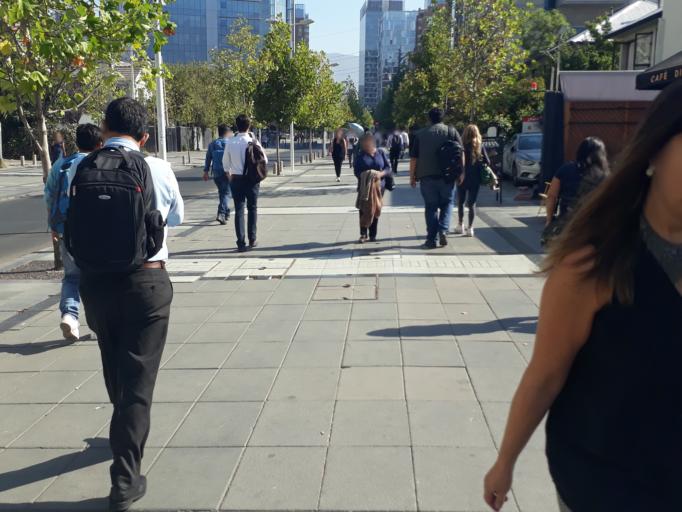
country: CL
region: Santiago Metropolitan
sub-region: Provincia de Santiago
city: Villa Presidente Frei, Nunoa, Santiago, Chile
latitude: -33.4089
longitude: -70.5708
